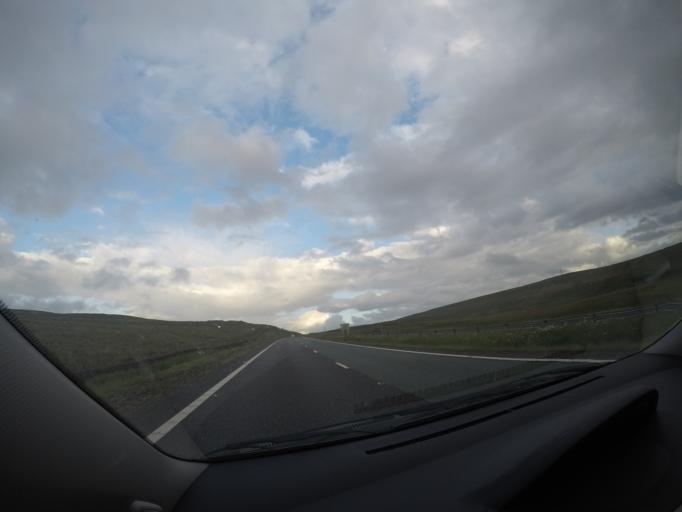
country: GB
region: England
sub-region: County Durham
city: Holwick
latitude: 54.5153
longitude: -2.2054
